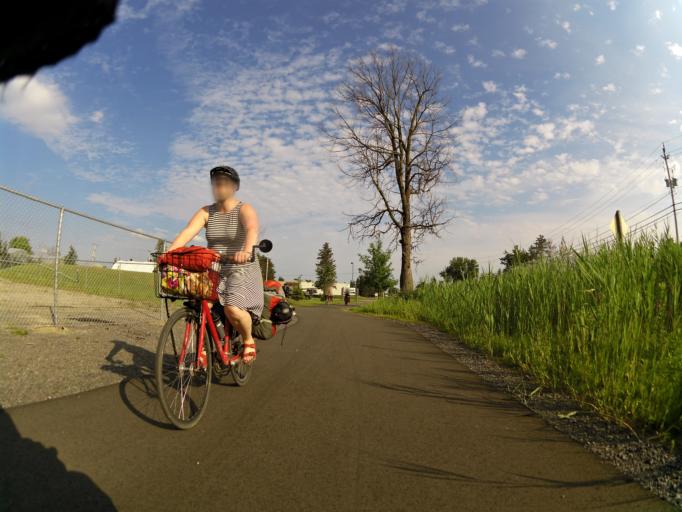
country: CA
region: Ontario
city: Bells Corners
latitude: 45.0258
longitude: -75.6568
